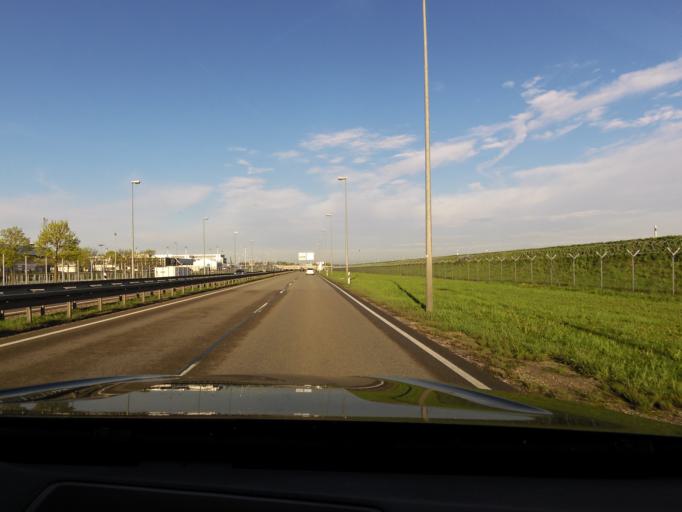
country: DE
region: Bavaria
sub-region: Upper Bavaria
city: Marzling
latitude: 48.3605
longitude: 11.8013
